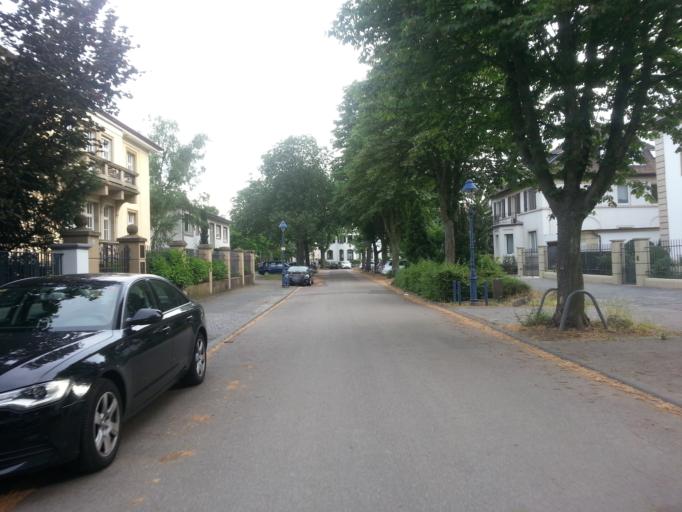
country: DE
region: Baden-Wuerttemberg
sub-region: Karlsruhe Region
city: Mannheim
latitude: 49.4828
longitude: 8.4879
